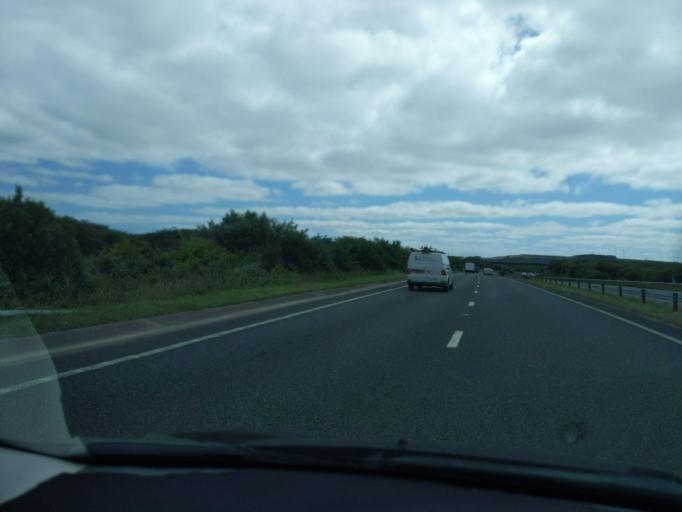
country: GB
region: England
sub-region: Cornwall
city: Saint Dennis
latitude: 50.4099
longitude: -4.8990
